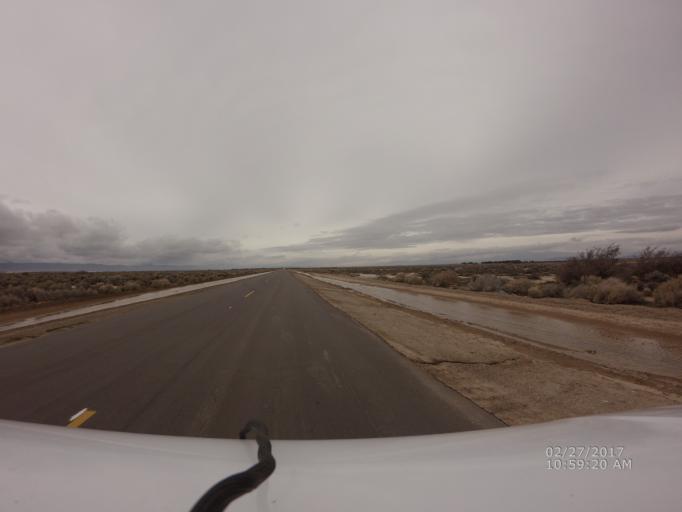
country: US
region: California
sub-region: Los Angeles County
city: Lancaster
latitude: 34.7479
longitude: -118.1509
